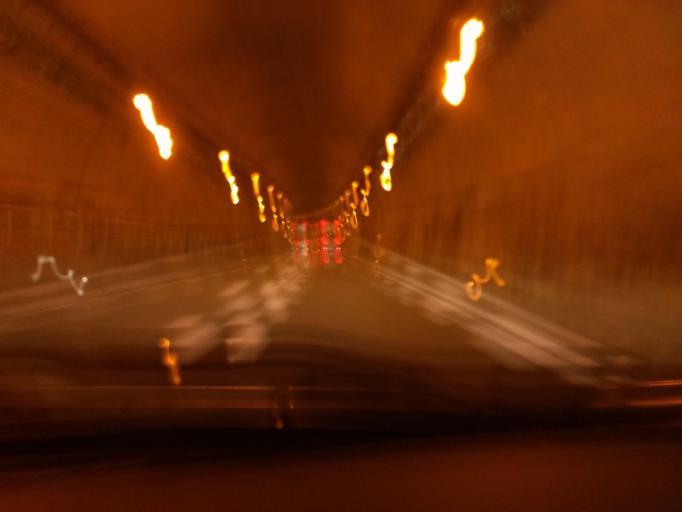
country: JP
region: Niigata
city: Kashiwazaki
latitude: 37.3432
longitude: 138.5153
